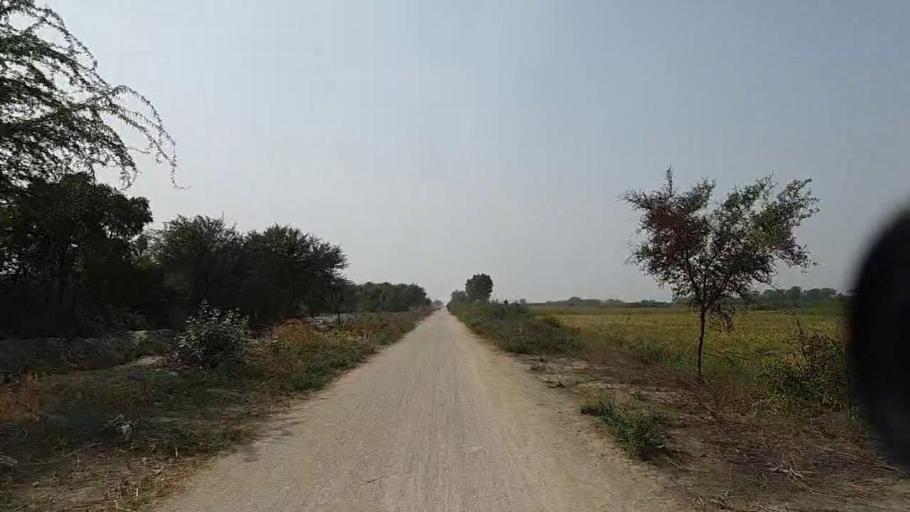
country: PK
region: Sindh
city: Naukot
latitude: 24.7694
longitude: 69.3454
